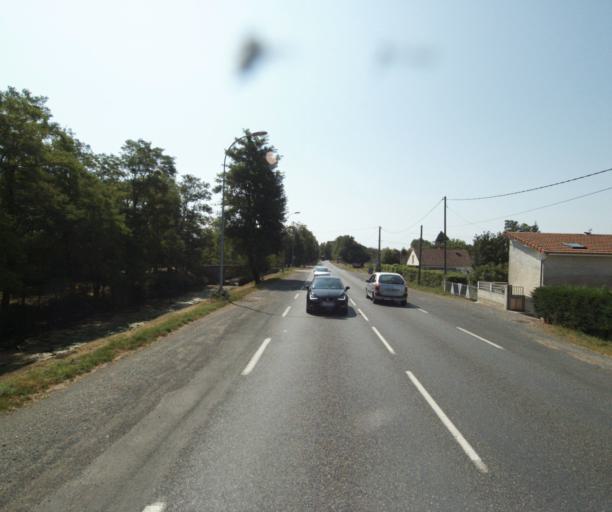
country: FR
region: Bourgogne
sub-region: Departement de Saone-et-Loire
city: Gueugnon
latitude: 46.5883
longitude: 4.0601
